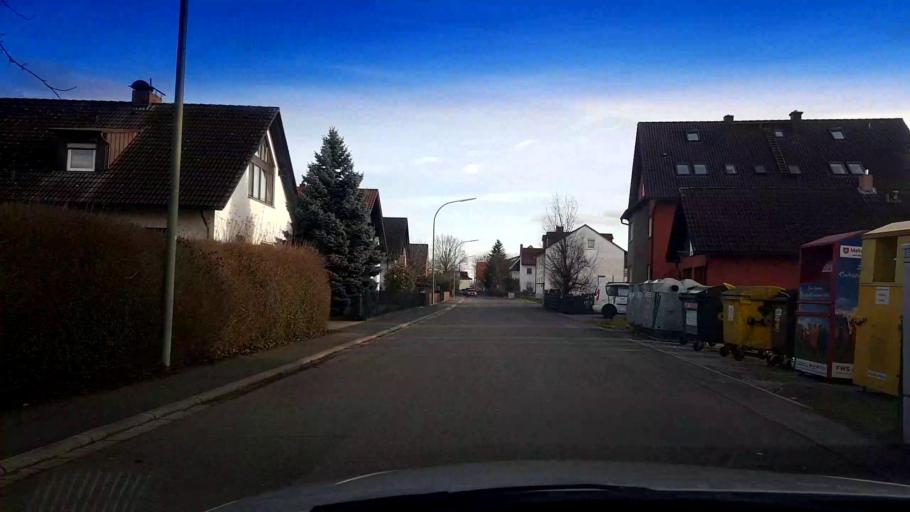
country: DE
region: Bavaria
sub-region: Upper Franconia
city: Strullendorf
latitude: 49.8425
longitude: 10.9668
